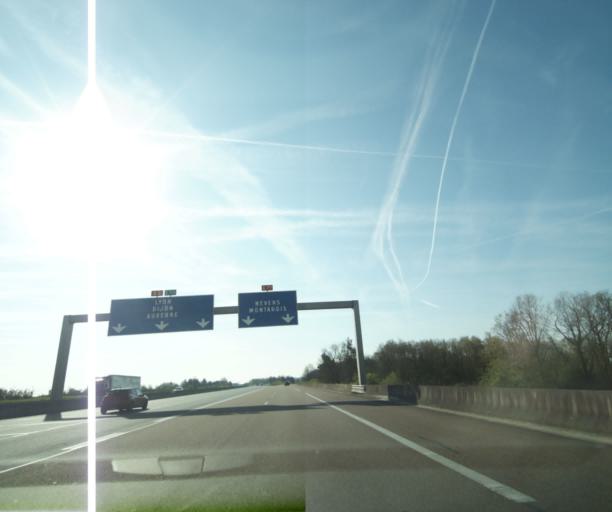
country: FR
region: Ile-de-France
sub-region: Departement de Seine-et-Marne
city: Souppes-sur-Loing
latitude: 48.2202
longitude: 2.7690
